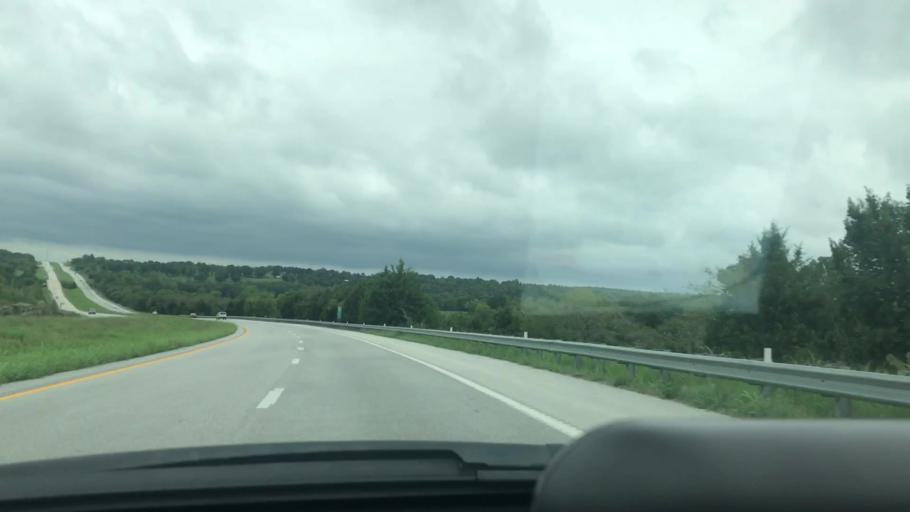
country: US
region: Missouri
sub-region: Greene County
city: Fair Grove
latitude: 37.4076
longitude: -93.1460
